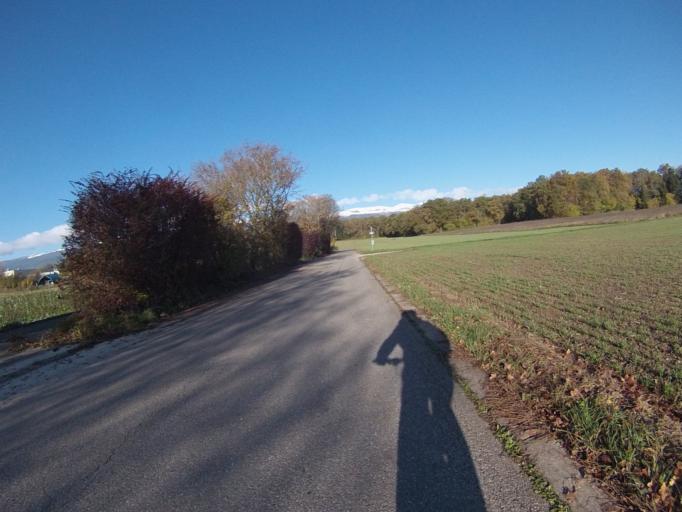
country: CH
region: Geneva
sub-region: Geneva
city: Meyrin
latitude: 46.2394
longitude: 6.0714
